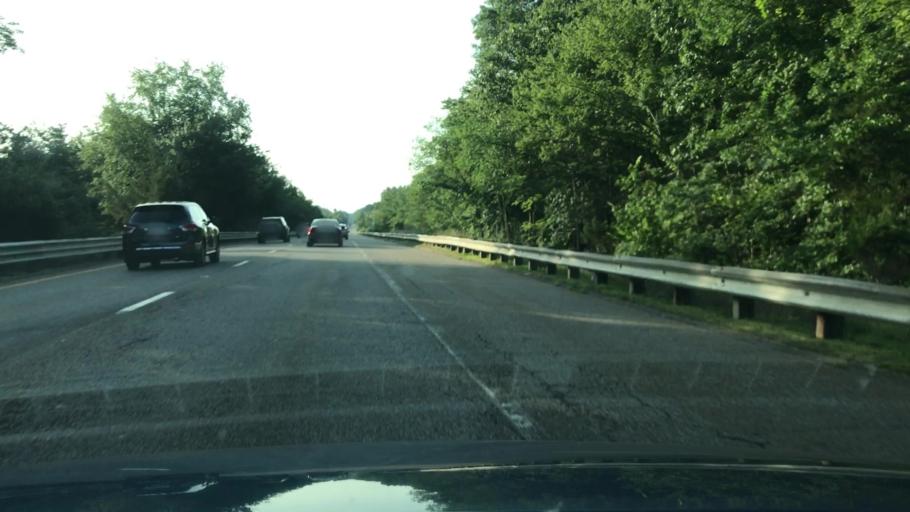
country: US
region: Massachusetts
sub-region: Plymouth County
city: Hanover
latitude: 42.1451
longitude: -70.8338
